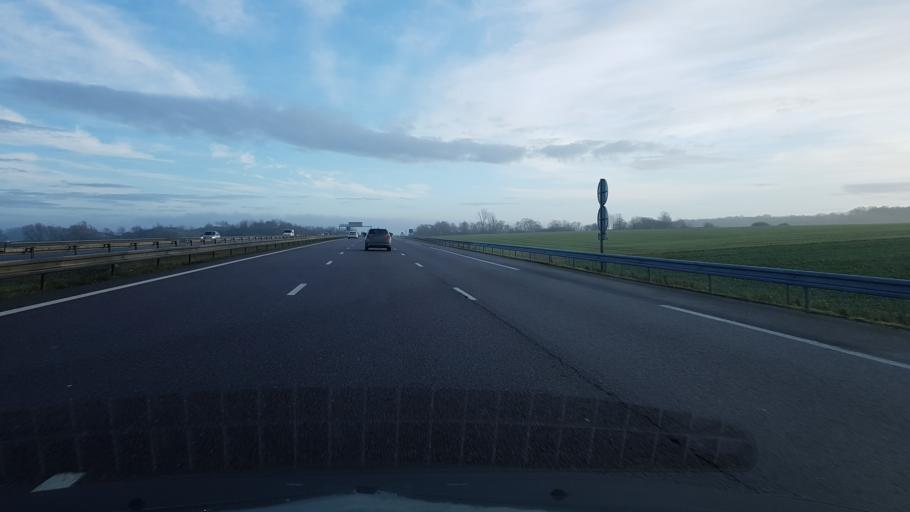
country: FR
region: Lorraine
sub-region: Departement de la Moselle
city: Retonfey
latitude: 49.1293
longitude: 6.3124
